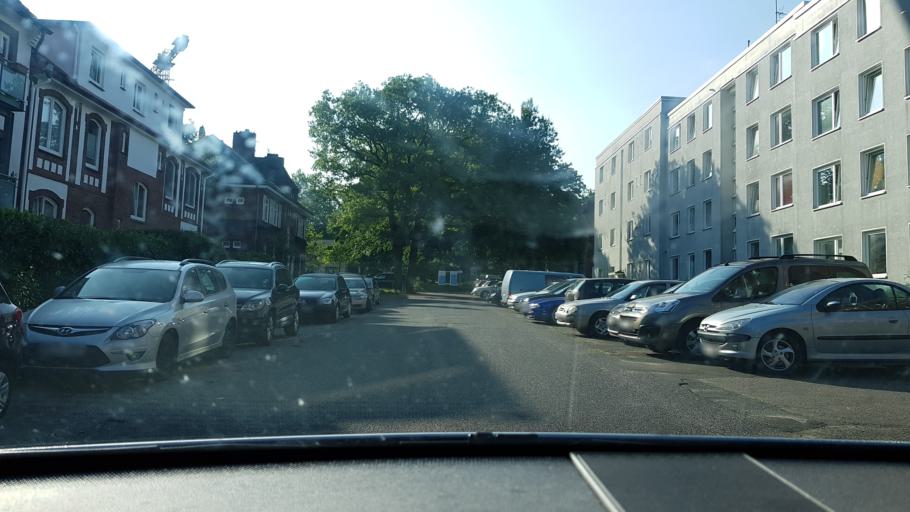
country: DE
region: Hamburg
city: Alsterdorf
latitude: 53.6154
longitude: 10.0243
